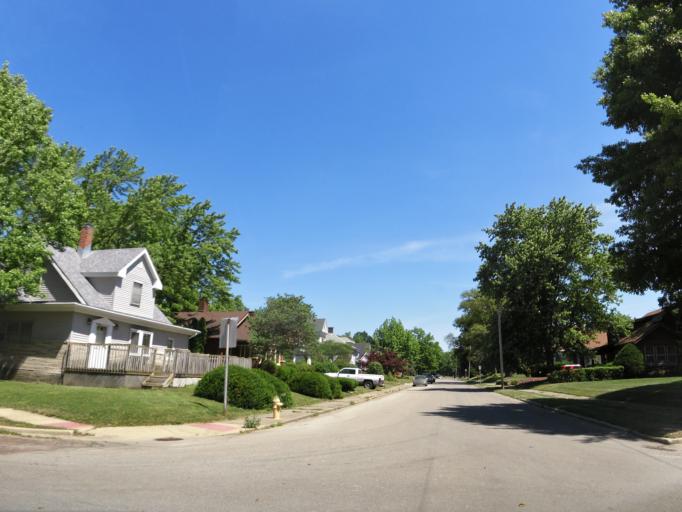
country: US
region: Illinois
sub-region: Vermilion County
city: Danville
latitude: 40.1475
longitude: -87.6316
